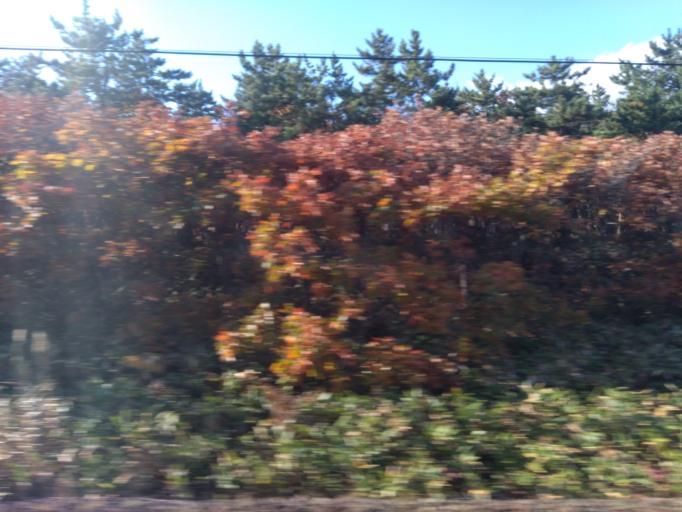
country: JP
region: Hokkaido
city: Niseko Town
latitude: 42.5626
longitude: 140.4322
